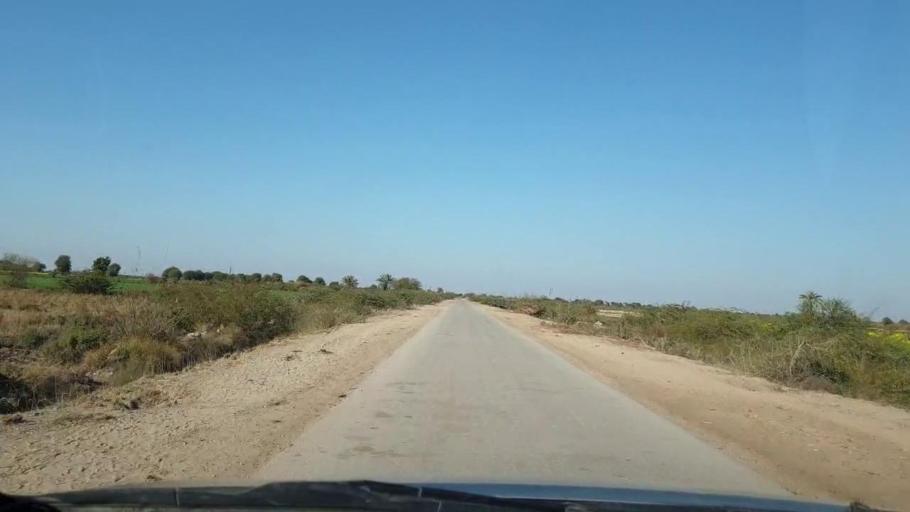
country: PK
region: Sindh
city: Jhol
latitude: 25.8391
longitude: 68.9513
